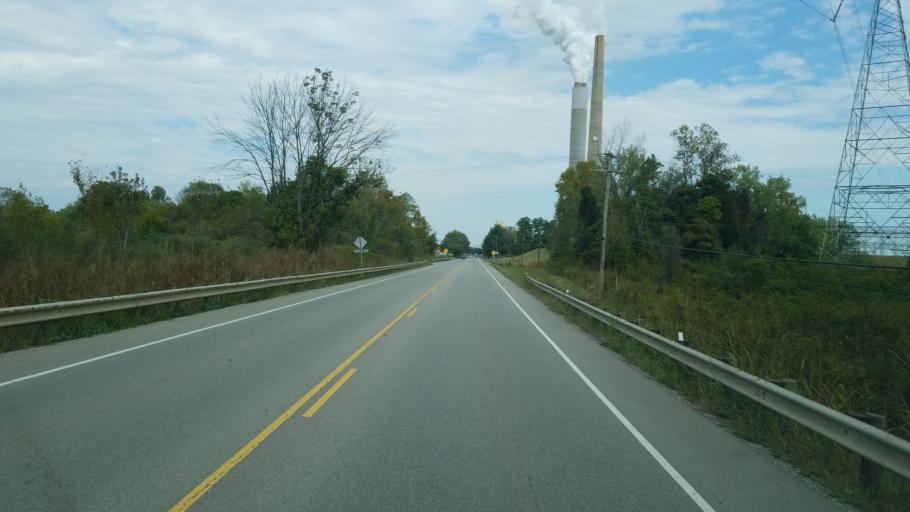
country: US
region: West Virginia
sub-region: Mason County
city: Point Pleasant
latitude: 38.9105
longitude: -82.1372
